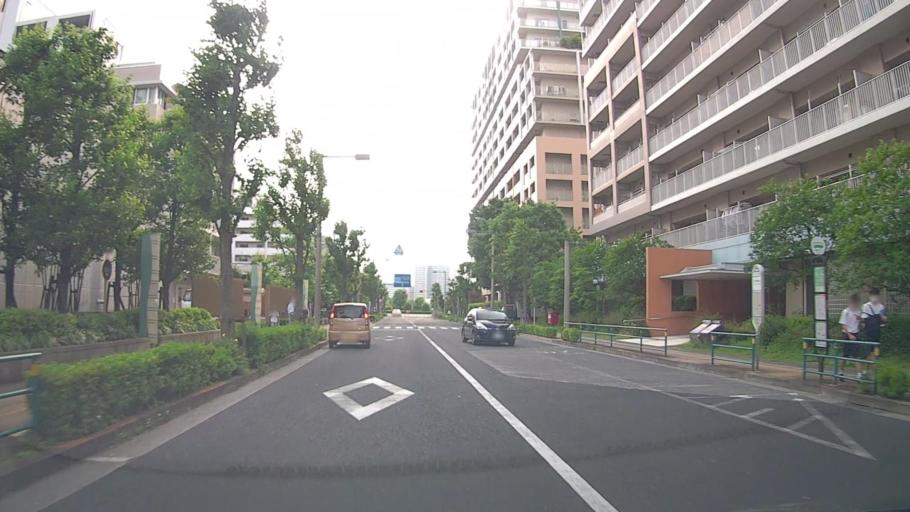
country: JP
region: Saitama
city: Kawaguchi
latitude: 35.7687
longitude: 139.7496
